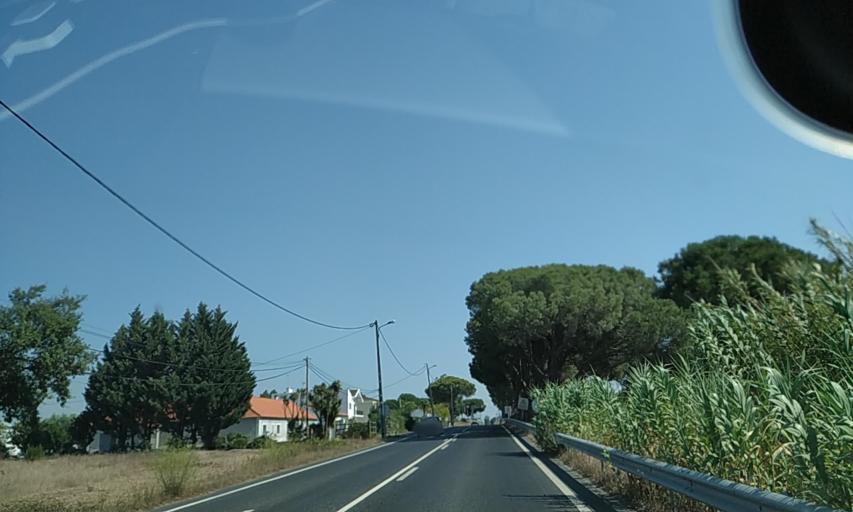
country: PT
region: Santarem
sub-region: Benavente
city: Poceirao
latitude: 38.7483
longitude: -8.6657
